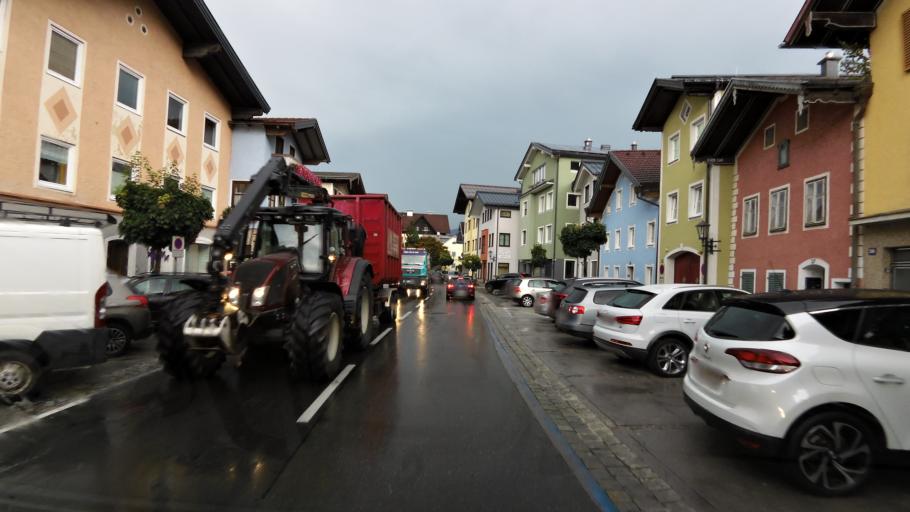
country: AT
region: Salzburg
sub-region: Politischer Bezirk Hallein
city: Golling an der Salzach
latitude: 47.5993
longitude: 13.1683
